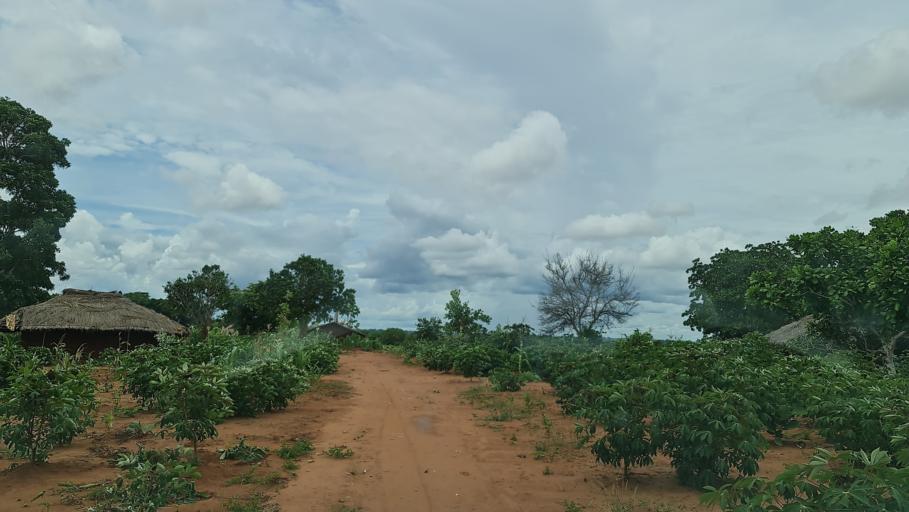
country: MZ
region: Nampula
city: Nacala
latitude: -14.7854
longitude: 39.9800
